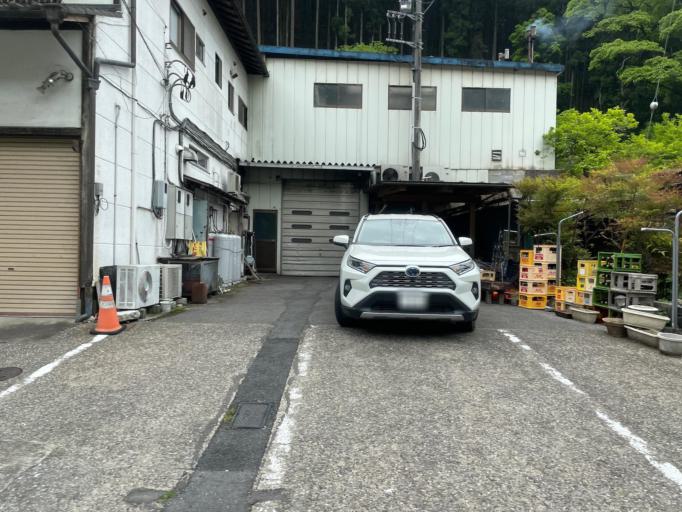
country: JP
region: Tochigi
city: Tanuma
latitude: 36.4704
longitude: 139.5964
